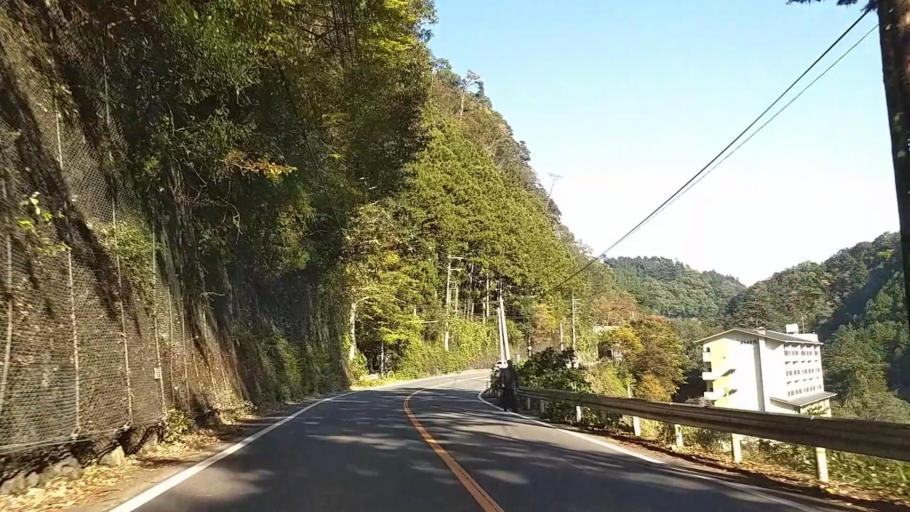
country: JP
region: Tokyo
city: Ome
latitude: 35.8132
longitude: 139.1252
